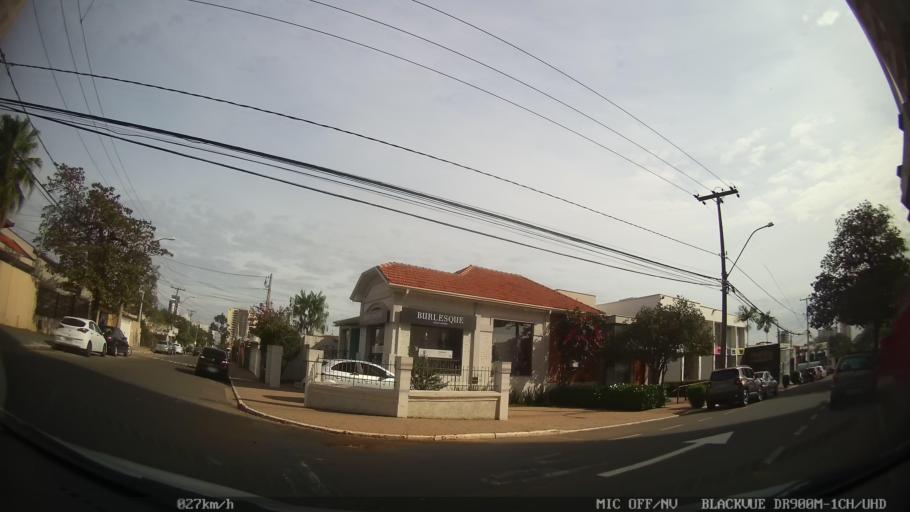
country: BR
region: Sao Paulo
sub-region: Piracicaba
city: Piracicaba
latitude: -22.7143
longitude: -47.6367
